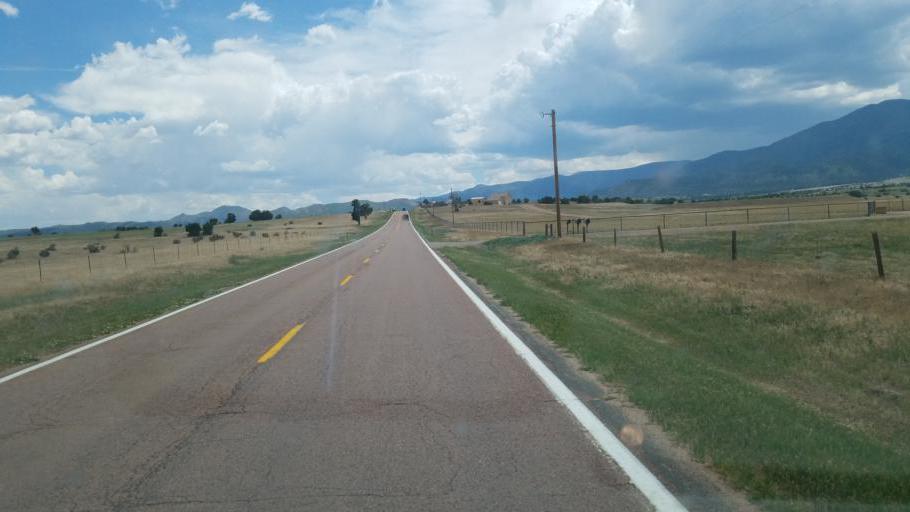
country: US
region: Colorado
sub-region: Fremont County
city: Florence
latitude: 38.2729
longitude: -105.0875
